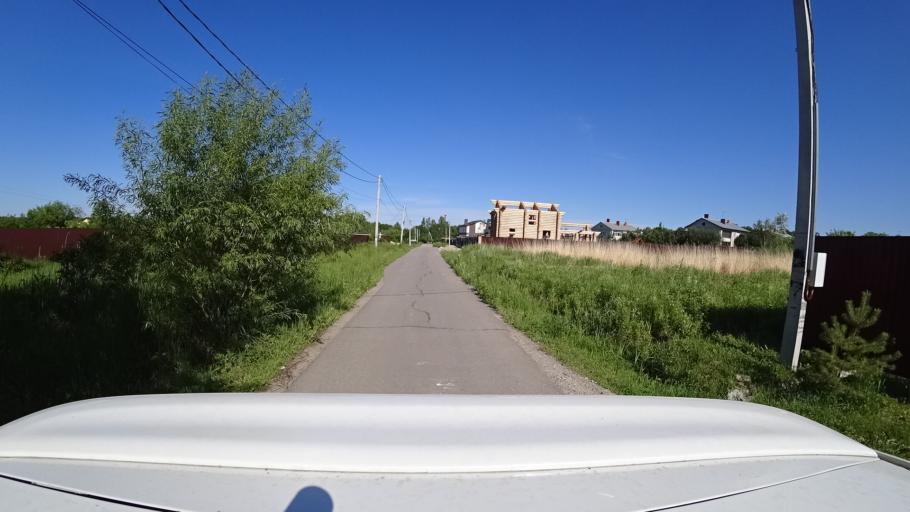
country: RU
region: Khabarovsk Krai
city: Topolevo
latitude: 48.5482
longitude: 135.1807
